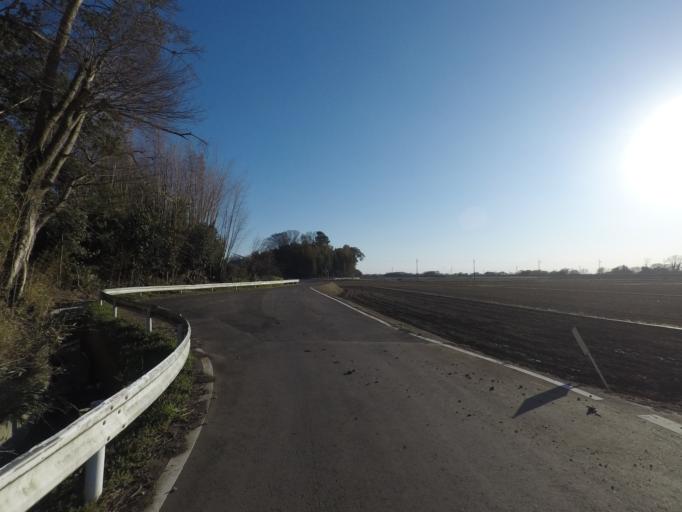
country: JP
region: Ibaraki
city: Ishige
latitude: 36.1420
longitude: 140.0077
